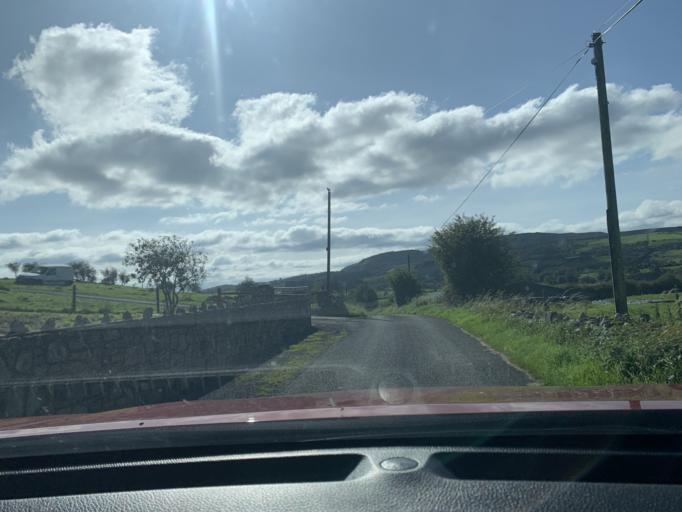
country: IE
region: Connaught
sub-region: Roscommon
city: Boyle
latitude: 54.0807
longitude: -8.3677
